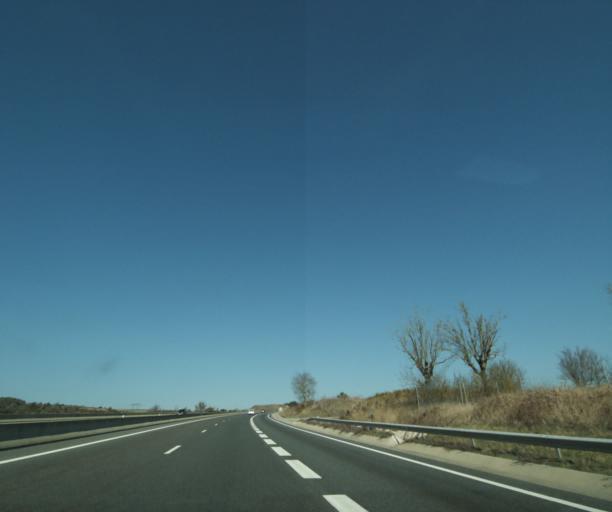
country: FR
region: Midi-Pyrenees
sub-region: Departement de l'Aveyron
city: Severac-le-Chateau
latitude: 44.2368
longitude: 3.0598
